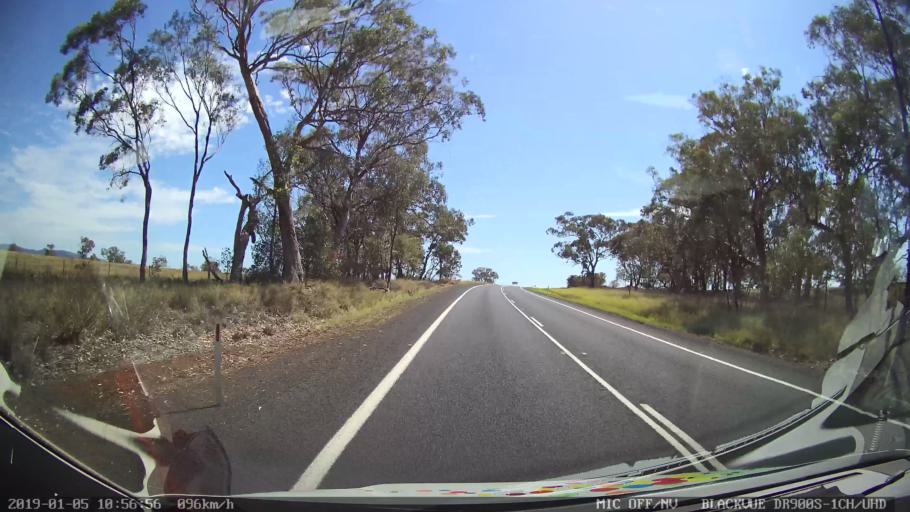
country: AU
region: New South Wales
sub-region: Warrumbungle Shire
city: Coonabarabran
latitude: -31.4358
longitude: 149.1635
